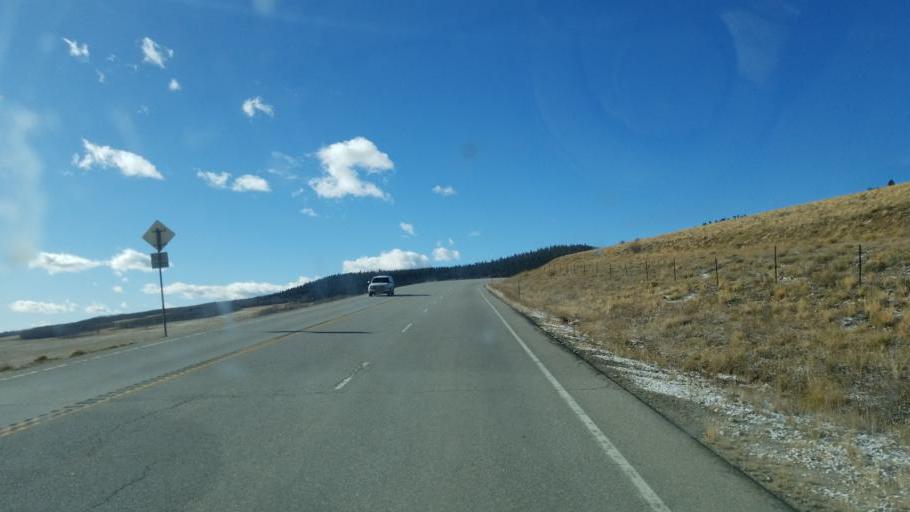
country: US
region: Colorado
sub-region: Park County
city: Fairplay
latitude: 39.2733
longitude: -105.9529
